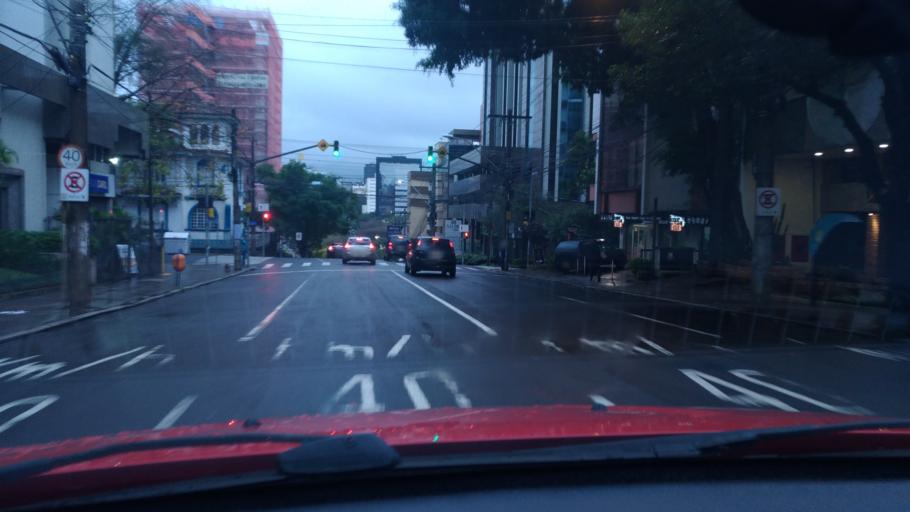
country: BR
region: Rio Grande do Sul
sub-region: Porto Alegre
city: Porto Alegre
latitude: -30.0287
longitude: -51.2036
